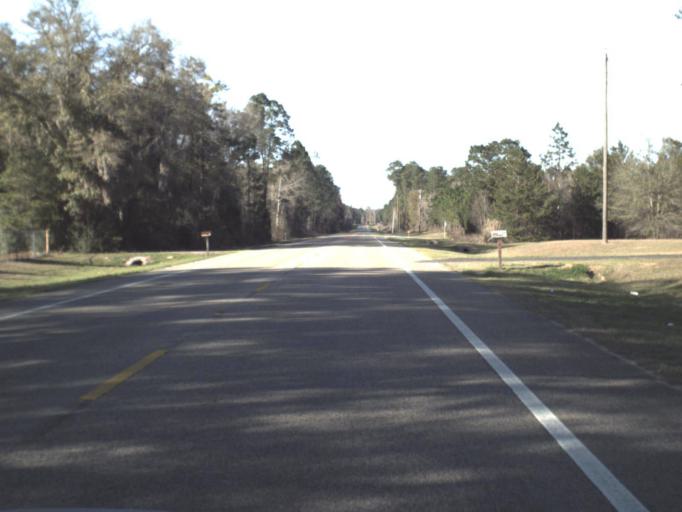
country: US
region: Florida
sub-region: Jackson County
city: Marianna
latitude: 30.6108
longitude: -85.1810
